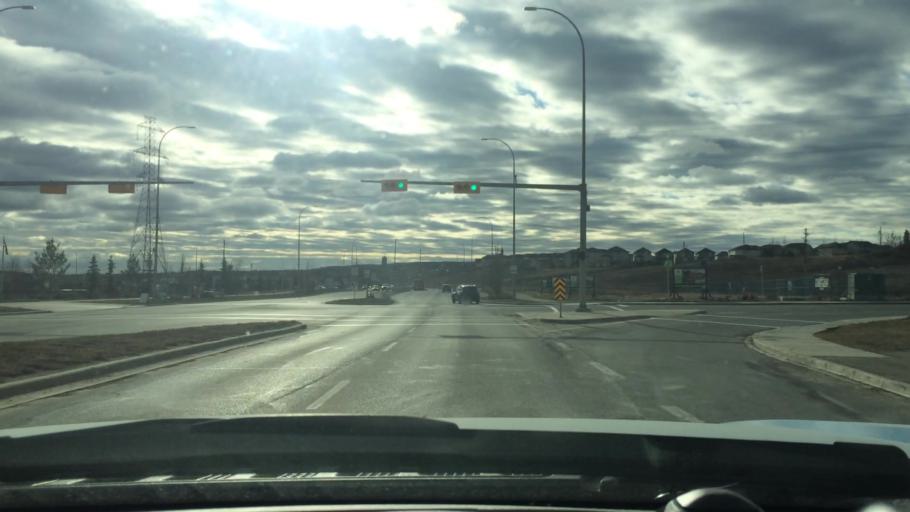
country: CA
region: Alberta
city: Calgary
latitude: 51.1702
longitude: -114.1333
